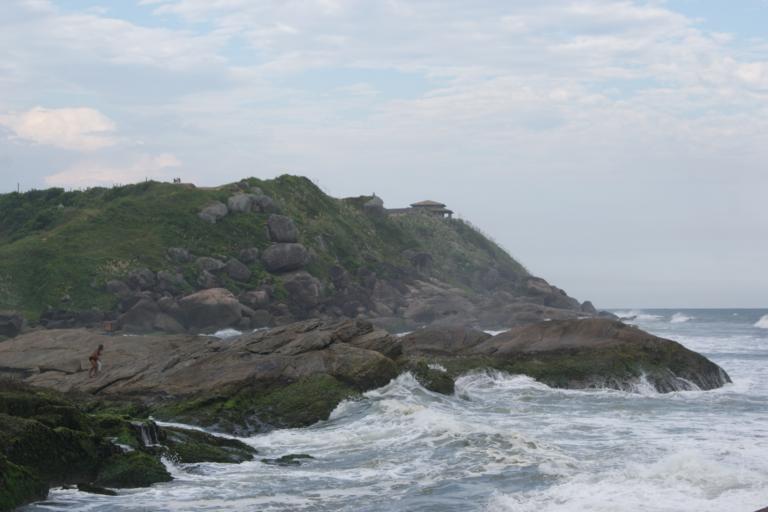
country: BR
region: Sao Paulo
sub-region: Itanhaem
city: Itanhaem
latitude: -24.2023
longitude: -46.8117
